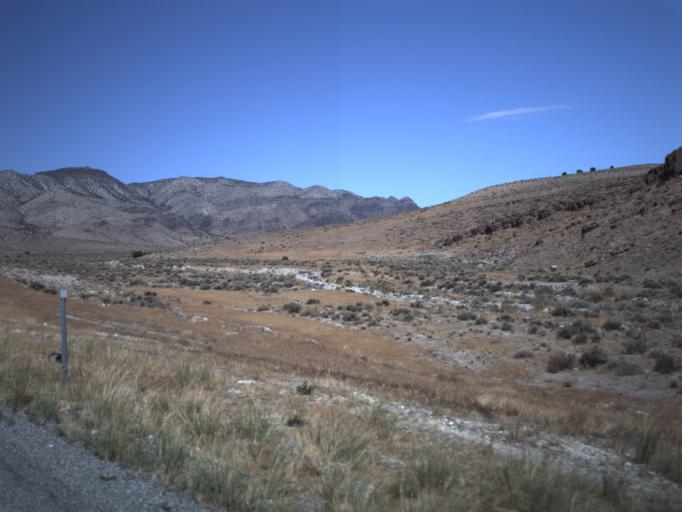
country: US
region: Utah
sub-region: Beaver County
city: Milford
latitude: 39.0852
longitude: -113.5181
